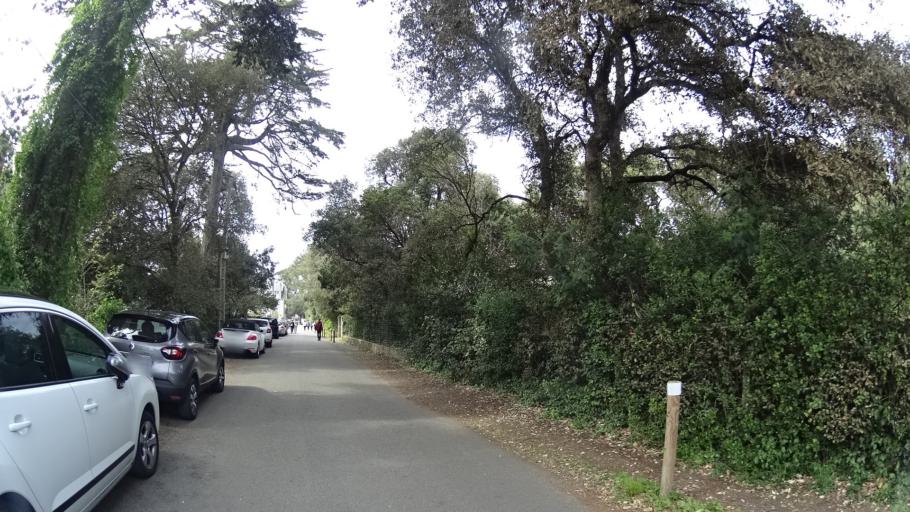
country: FR
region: Pays de la Loire
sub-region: Departement de la Vendee
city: La Gueriniere
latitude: 47.0100
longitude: -2.2253
